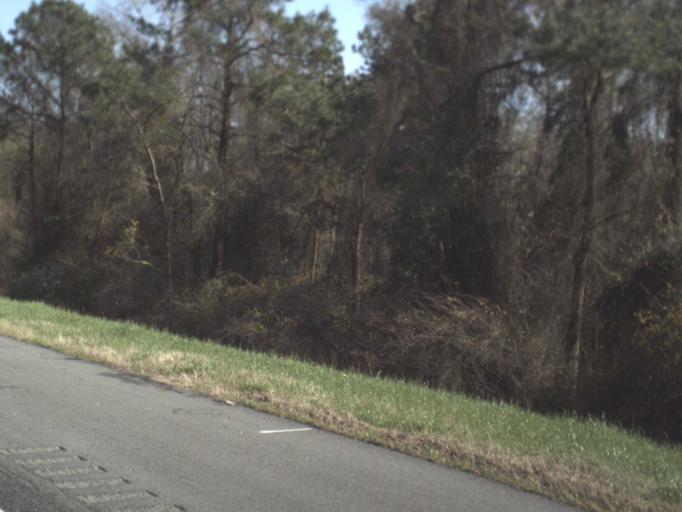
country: US
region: Florida
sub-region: Gadsden County
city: Gretna
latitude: 30.6108
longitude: -84.7522
